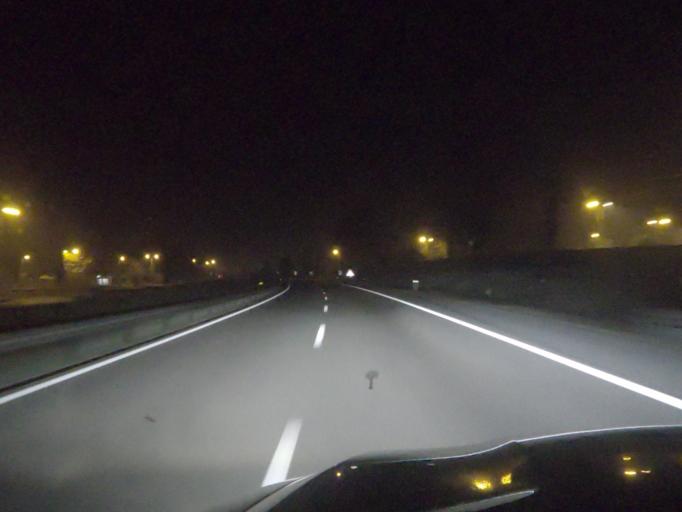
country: PT
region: Aveiro
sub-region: Oliveira do Bairro
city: Oia
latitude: 40.5495
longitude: -8.5601
